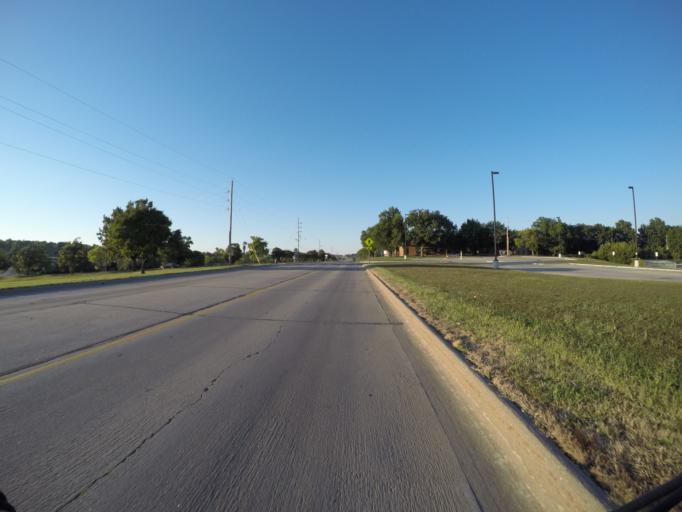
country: US
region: Kansas
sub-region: Riley County
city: Manhattan
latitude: 39.1978
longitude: -96.6167
